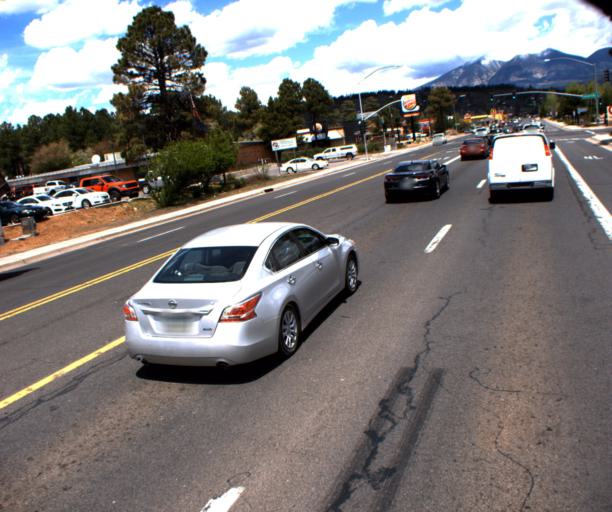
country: US
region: Arizona
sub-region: Coconino County
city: Flagstaff
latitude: 35.1826
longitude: -111.6613
